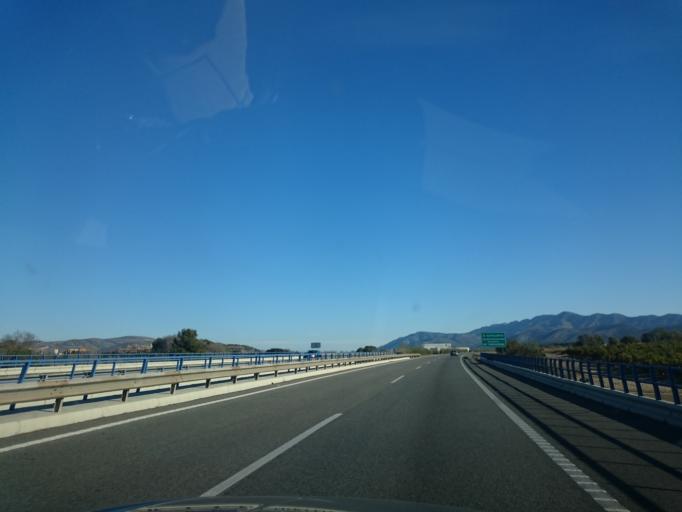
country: ES
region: Catalonia
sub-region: Provincia de Tarragona
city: Ulldecona
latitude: 40.5722
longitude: 0.4380
